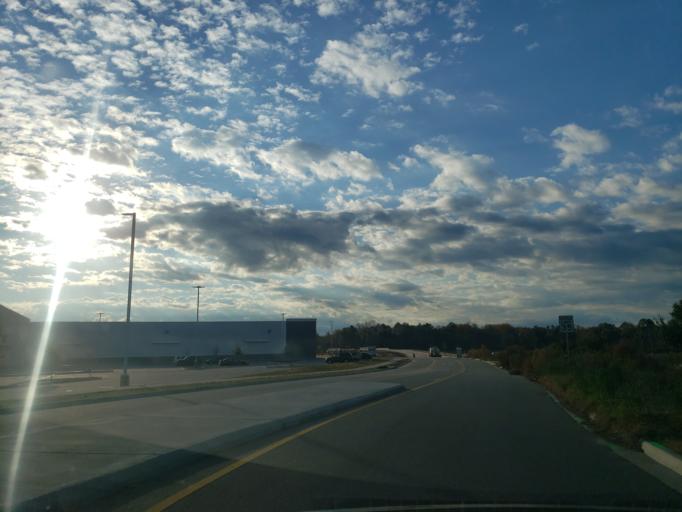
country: US
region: Georgia
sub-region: Chatham County
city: Pooler
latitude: 32.1318
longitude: -81.2483
